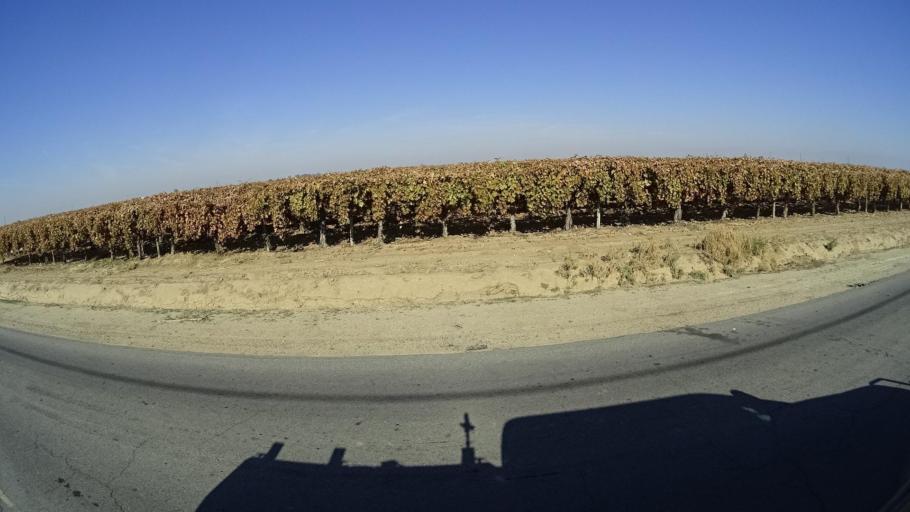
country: US
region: California
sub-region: Kern County
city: McFarland
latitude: 35.7180
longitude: -119.1646
